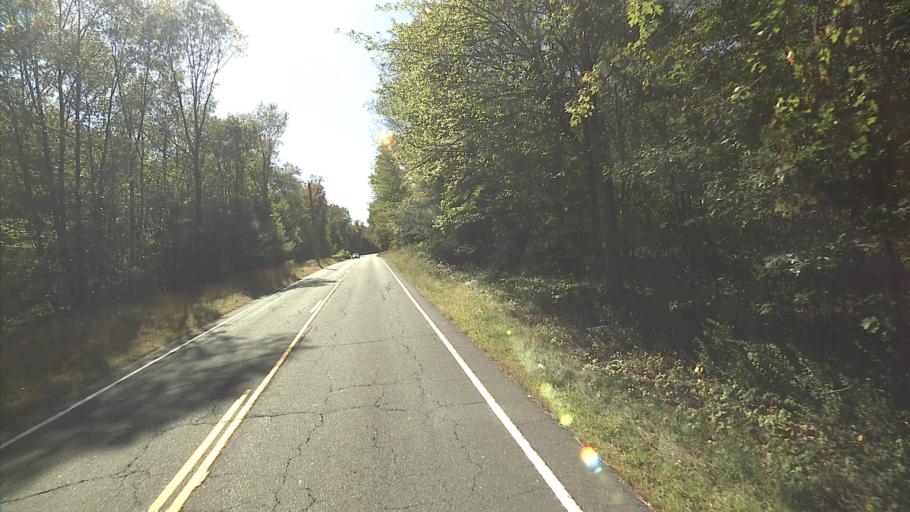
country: US
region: Connecticut
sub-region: Litchfield County
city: Terryville
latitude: 41.7469
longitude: -72.9738
